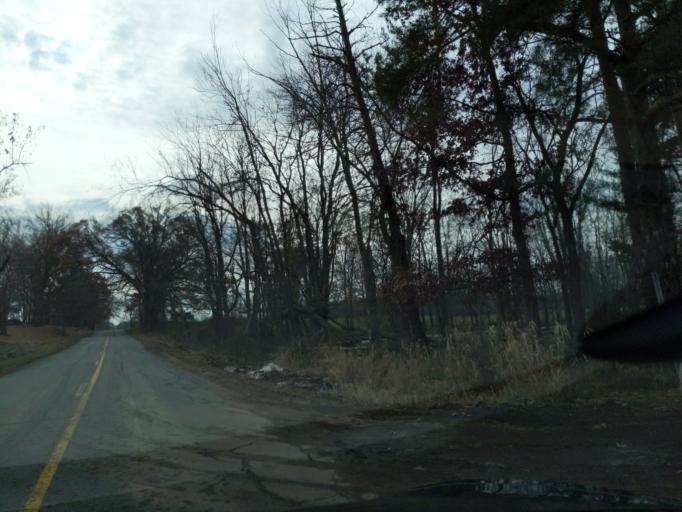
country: US
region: Michigan
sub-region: Ingham County
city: Leslie
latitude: 42.4597
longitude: -84.5019
